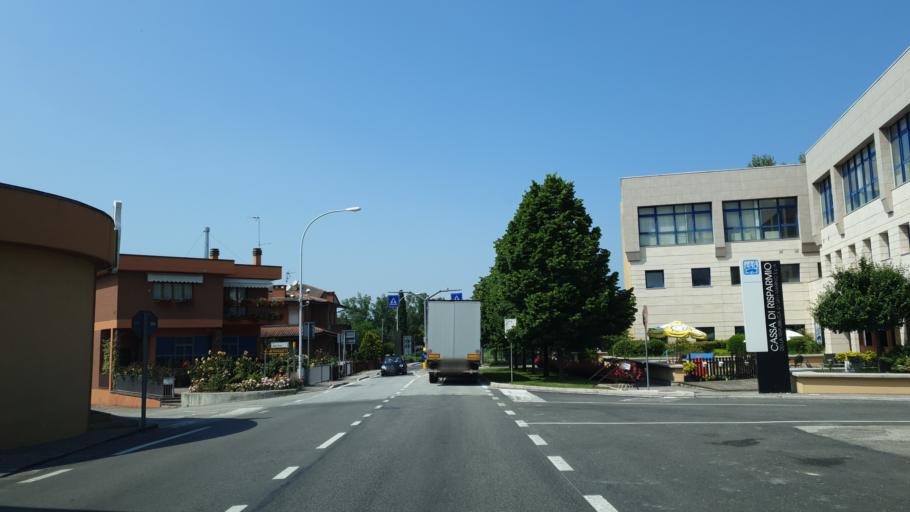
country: SM
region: Acquaviva
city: Acquaviva
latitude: 43.9538
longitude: 12.4055
